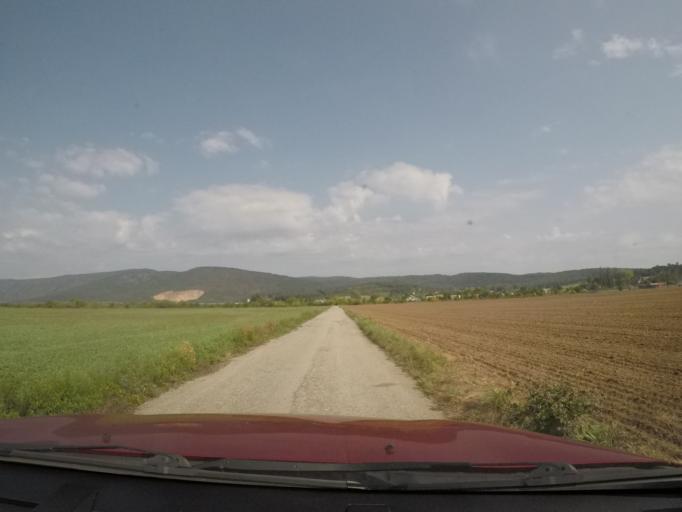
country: SK
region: Kosicky
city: Moldava nad Bodvou
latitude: 48.6020
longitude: 20.9532
